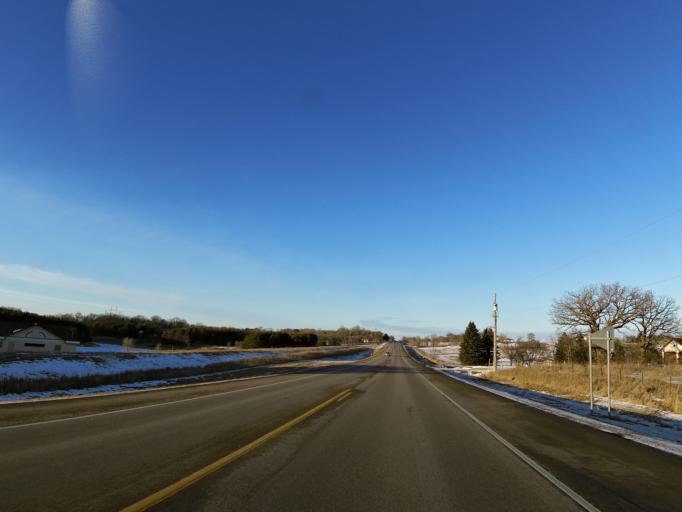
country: US
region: Minnesota
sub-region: Washington County
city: Cottage Grove
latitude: 44.8685
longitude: -92.9033
